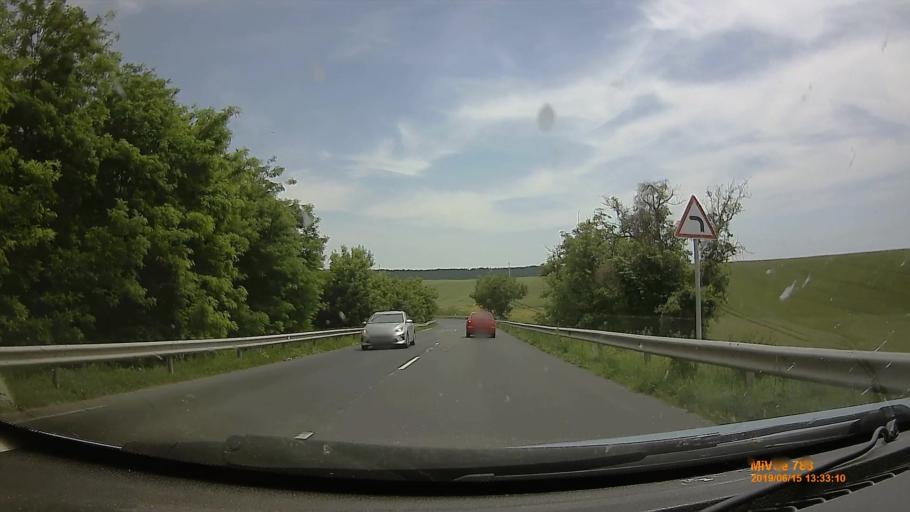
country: HU
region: Tolna
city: Tamasi
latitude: 46.5831
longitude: 18.2043
